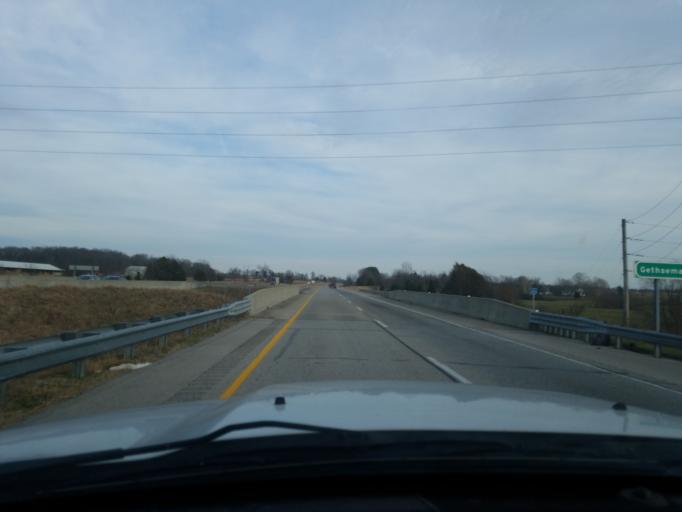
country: US
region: Indiana
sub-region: Harrison County
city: Corydon
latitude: 38.2415
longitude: -86.1827
